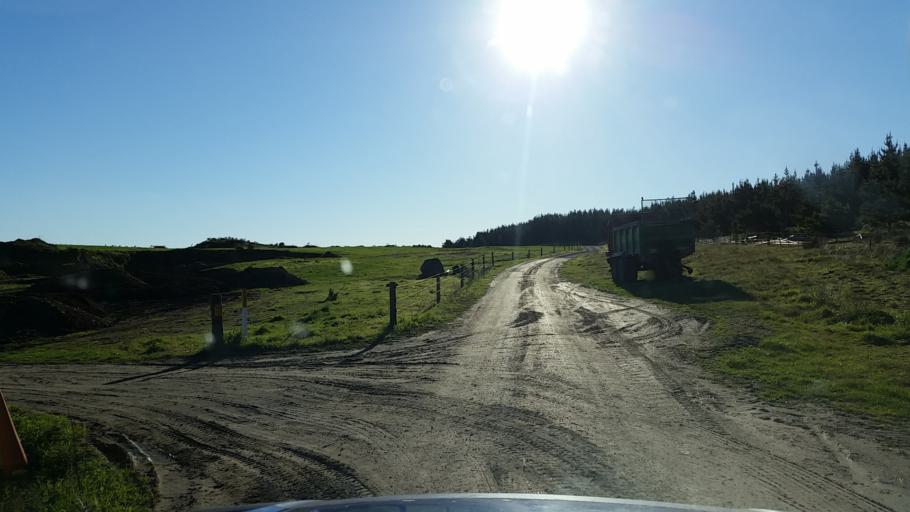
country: NZ
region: Taranaki
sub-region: South Taranaki District
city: Patea
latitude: -39.8349
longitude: 174.6838
